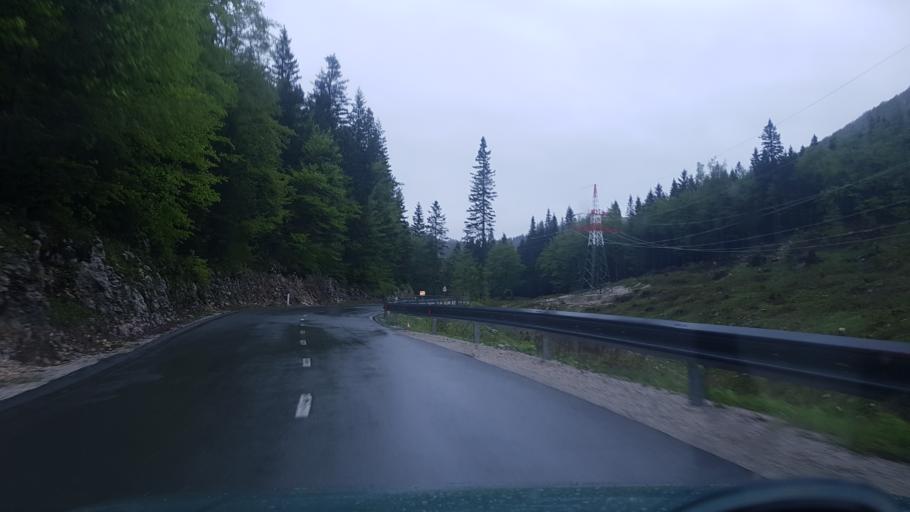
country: SI
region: Bohinj
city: Bohinjska Bistrica
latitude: 46.2468
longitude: 14.0057
